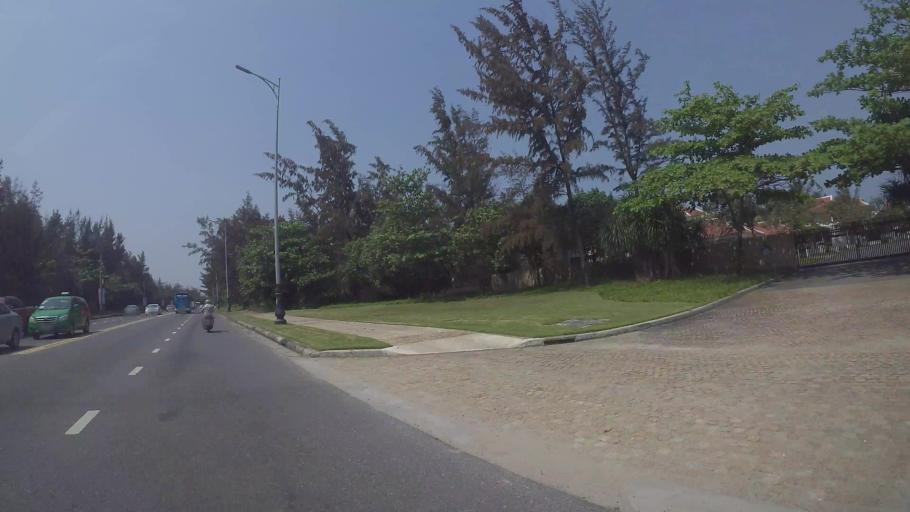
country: VN
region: Da Nang
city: Ngu Hanh Son
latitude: 15.9757
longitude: 108.2789
